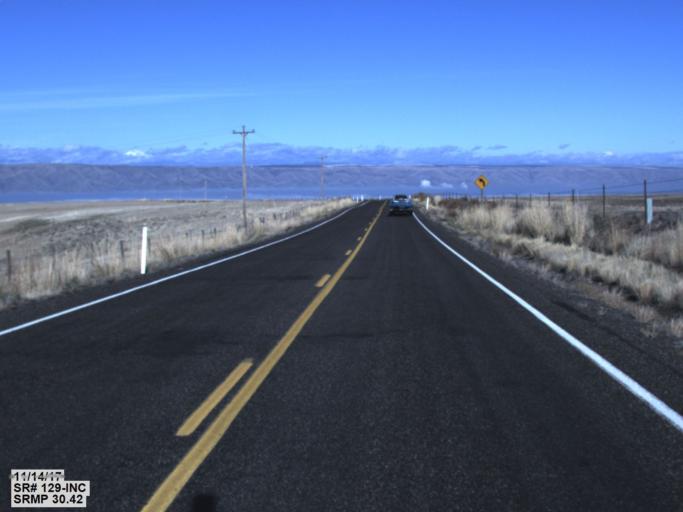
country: US
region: Washington
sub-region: Asotin County
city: Asotin
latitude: 46.2972
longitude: -117.0445
